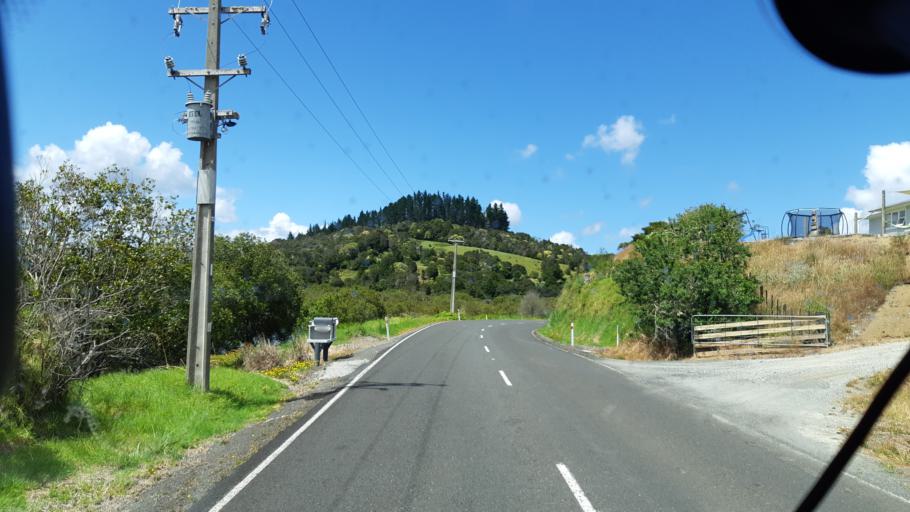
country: NZ
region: Northland
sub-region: Far North District
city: Taipa
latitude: -35.2739
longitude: 173.5215
